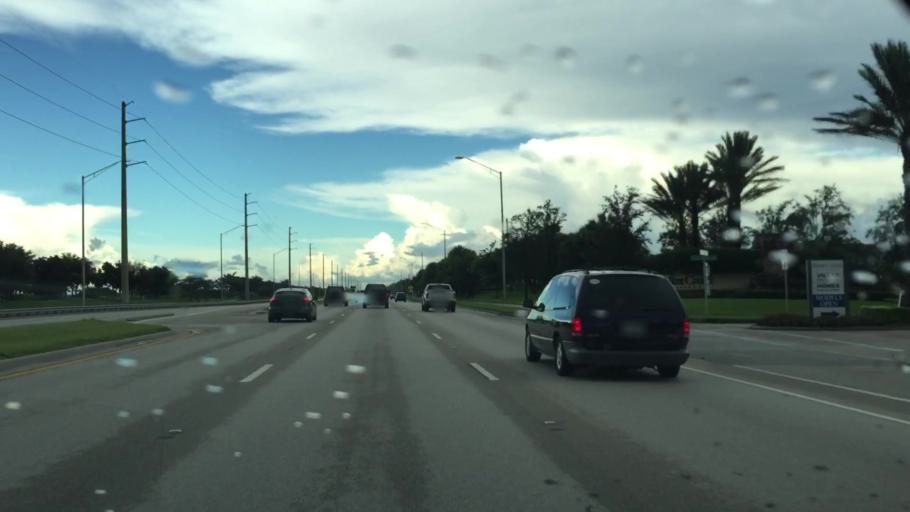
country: US
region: Florida
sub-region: Collier County
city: Vineyards
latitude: 26.2730
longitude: -81.6774
